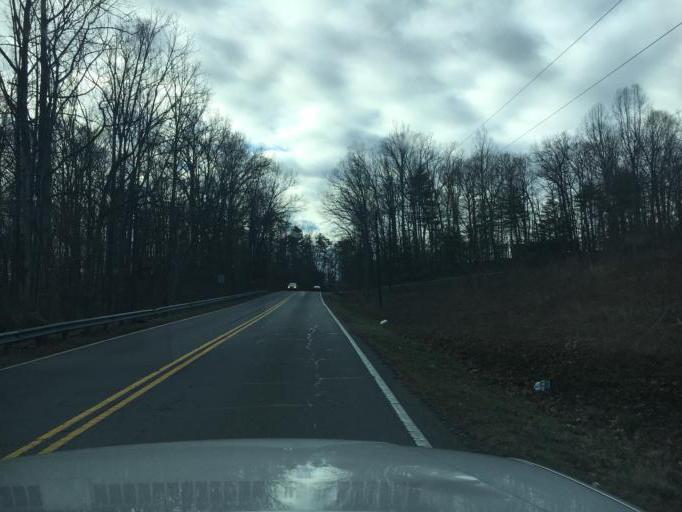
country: US
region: North Carolina
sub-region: Burke County
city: Salem
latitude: 35.6965
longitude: -81.7174
